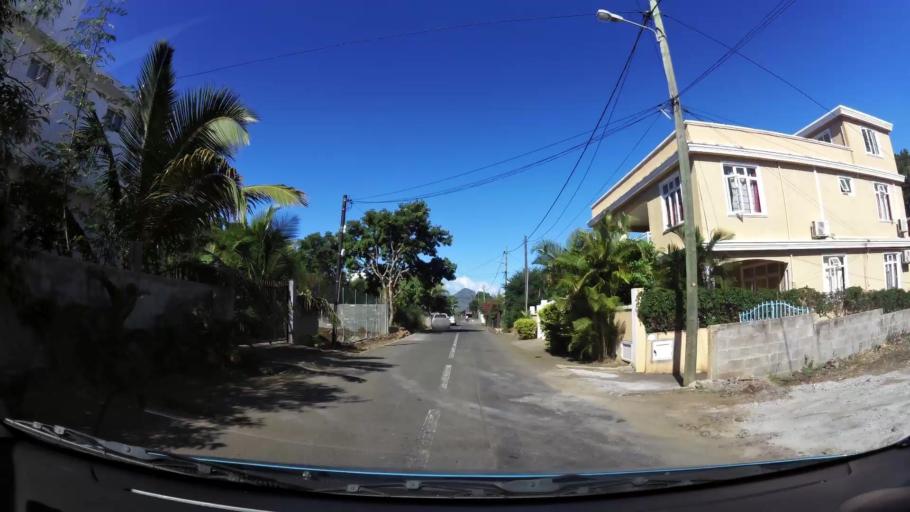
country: MU
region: Black River
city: Flic en Flac
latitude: -20.2770
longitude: 57.3758
